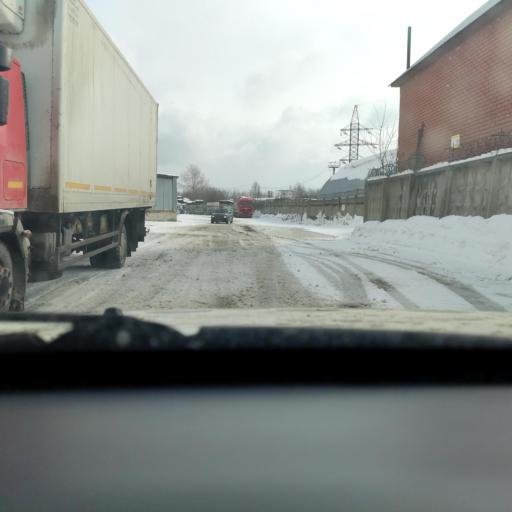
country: RU
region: Perm
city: Froly
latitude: 57.9559
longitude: 56.2452
